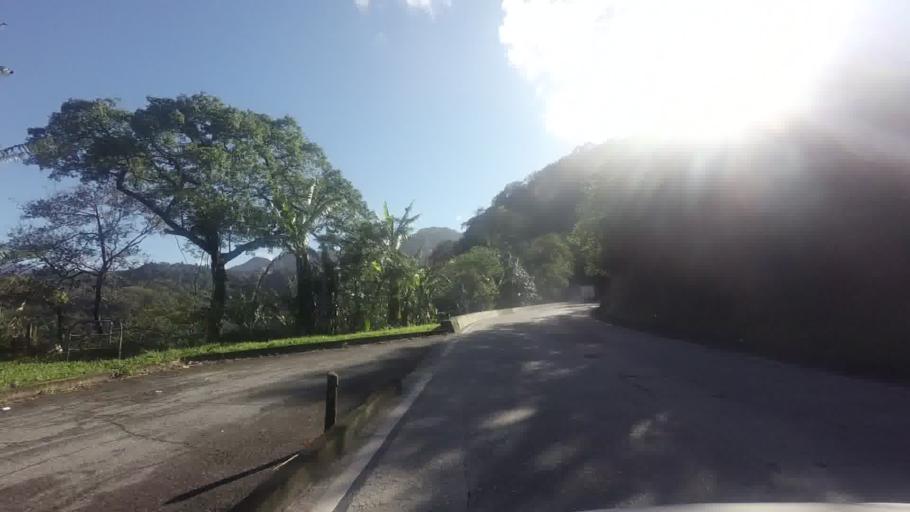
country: BR
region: Rio de Janeiro
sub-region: Petropolis
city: Petropolis
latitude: -22.5682
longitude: -43.2412
